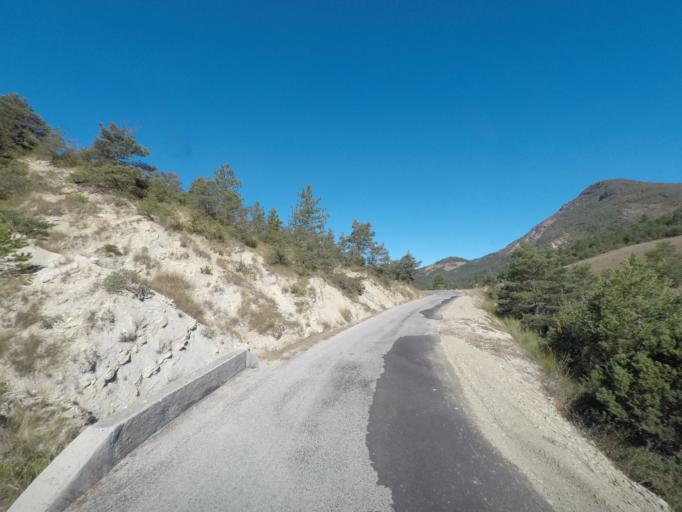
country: FR
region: Rhone-Alpes
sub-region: Departement de la Drome
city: Die
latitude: 44.5604
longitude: 5.3212
